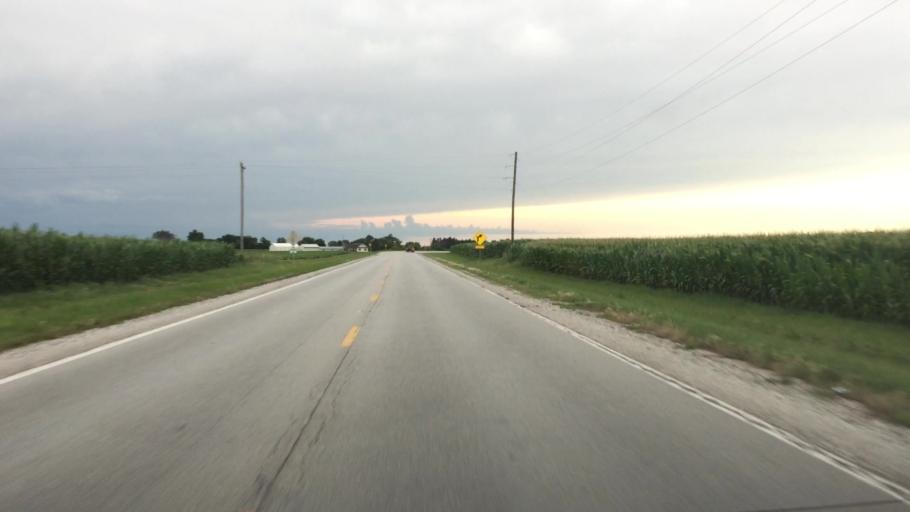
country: US
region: Illinois
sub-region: Hancock County
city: Hamilton
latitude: 40.3687
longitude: -91.3422
